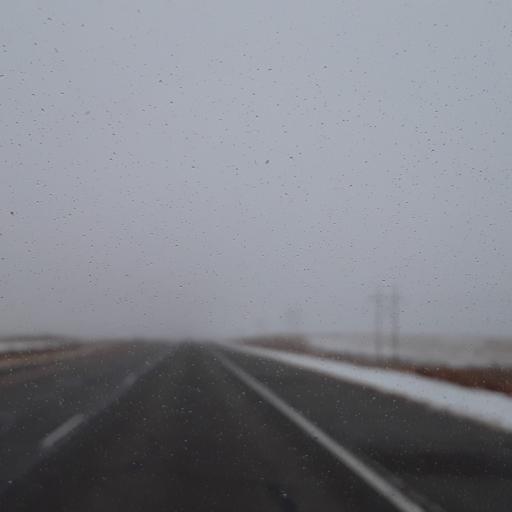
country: US
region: Nebraska
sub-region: Cheyenne County
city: Sidney
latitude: 40.8003
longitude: -102.8677
